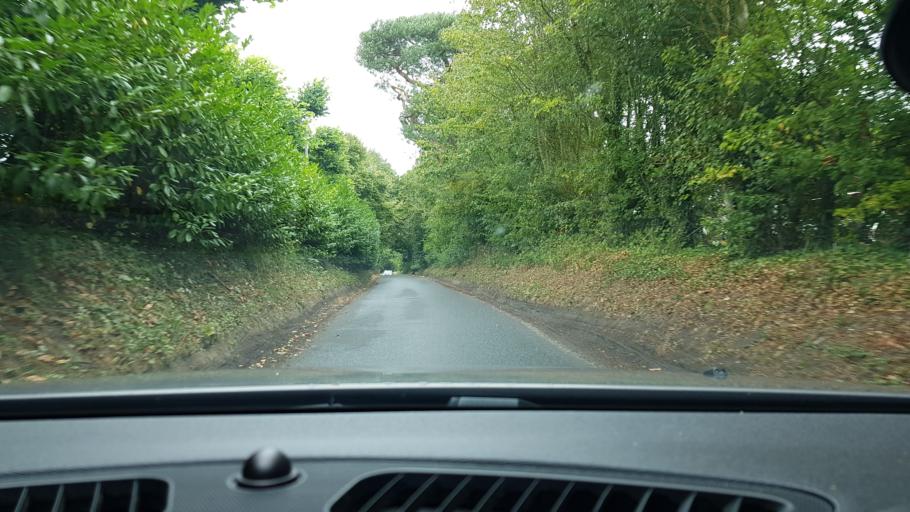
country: GB
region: England
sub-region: Wiltshire
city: Shalbourne
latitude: 51.3668
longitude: -1.5276
